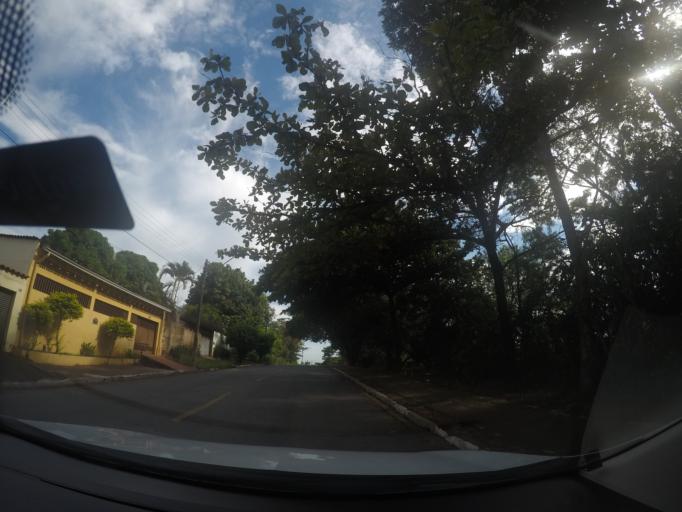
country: BR
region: Goias
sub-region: Goiania
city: Goiania
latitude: -16.6903
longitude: -49.2037
